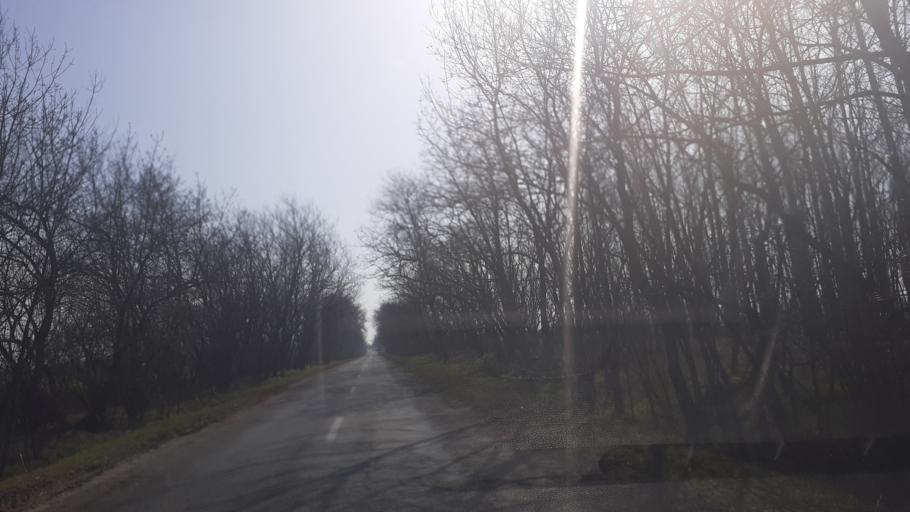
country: HU
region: Pest
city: Orkeny
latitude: 47.0922
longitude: 19.3618
